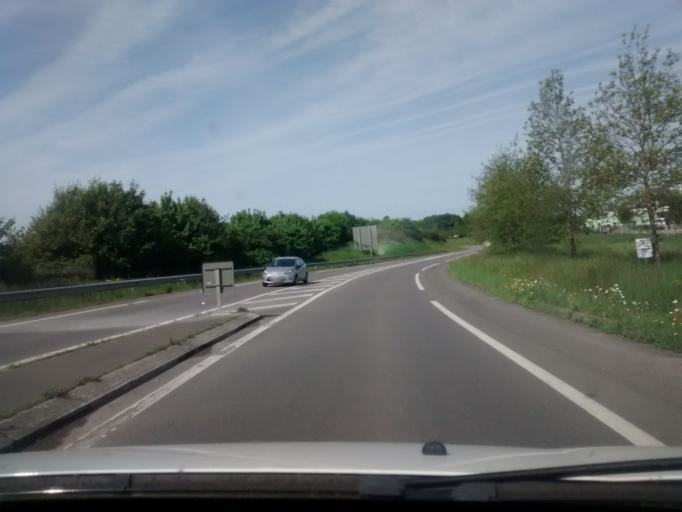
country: FR
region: Brittany
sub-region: Departement d'Ille-et-Vilaine
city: Saint-Etienne-en-Cogles
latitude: 48.3970
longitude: -1.3126
